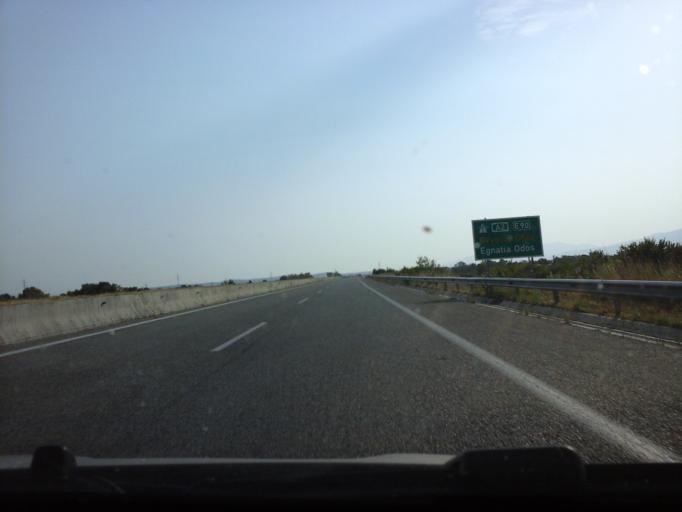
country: GR
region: East Macedonia and Thrace
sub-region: Nomos Xanthis
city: Peteinos
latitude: 41.0875
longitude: 24.9244
